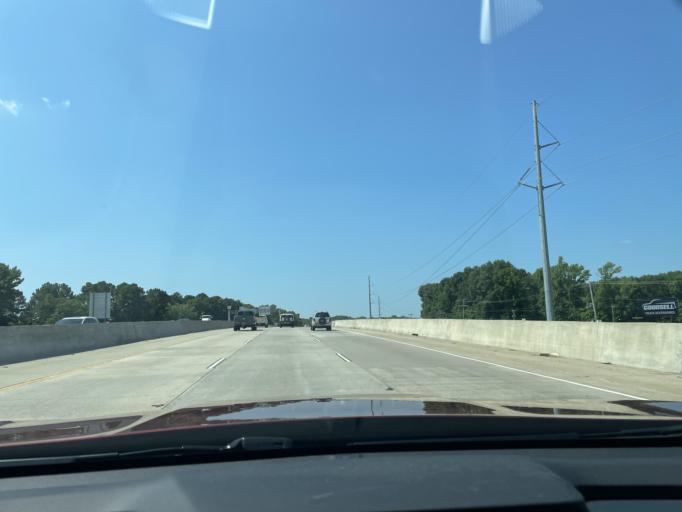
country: US
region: Arkansas
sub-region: Pulaski County
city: Jacksonville
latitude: 34.8630
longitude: -92.1295
